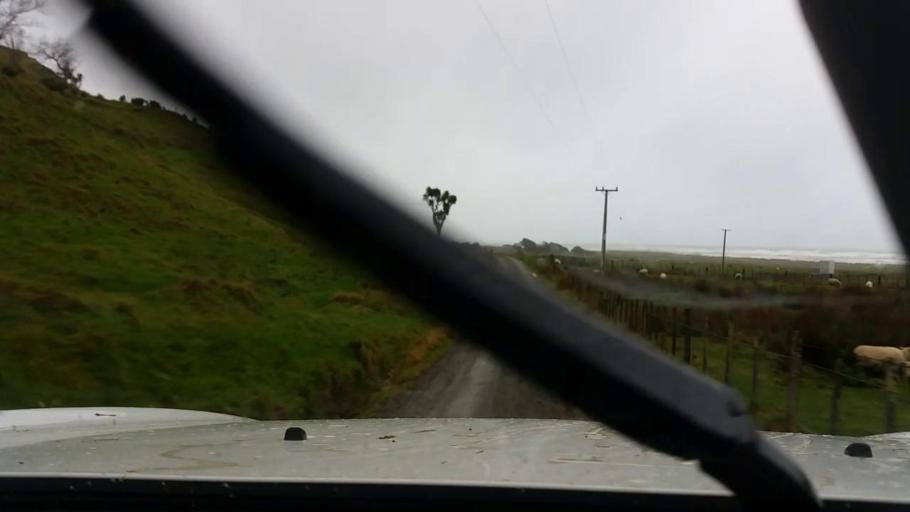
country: NZ
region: Wellington
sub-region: Masterton District
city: Masterton
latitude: -41.2646
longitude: 175.8898
